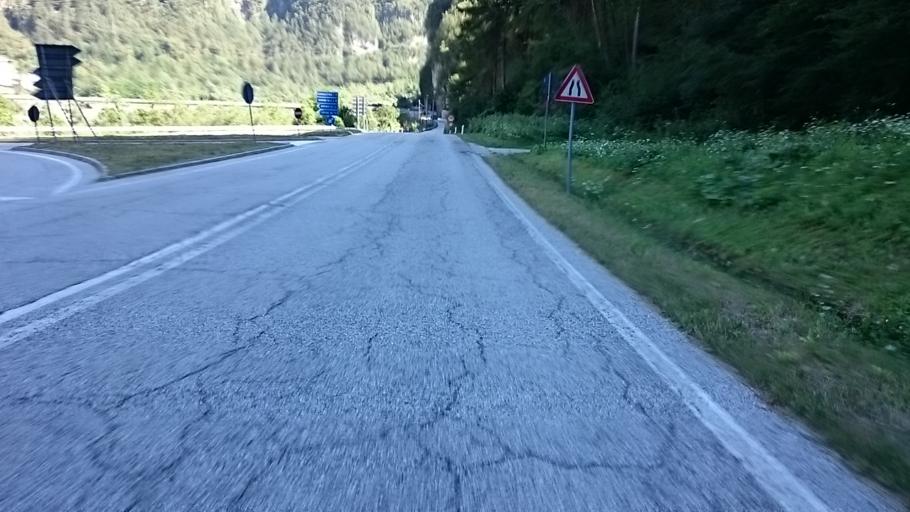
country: IT
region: Veneto
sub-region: Provincia di Belluno
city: Ospitale di Cadore
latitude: 46.3169
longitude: 12.3174
